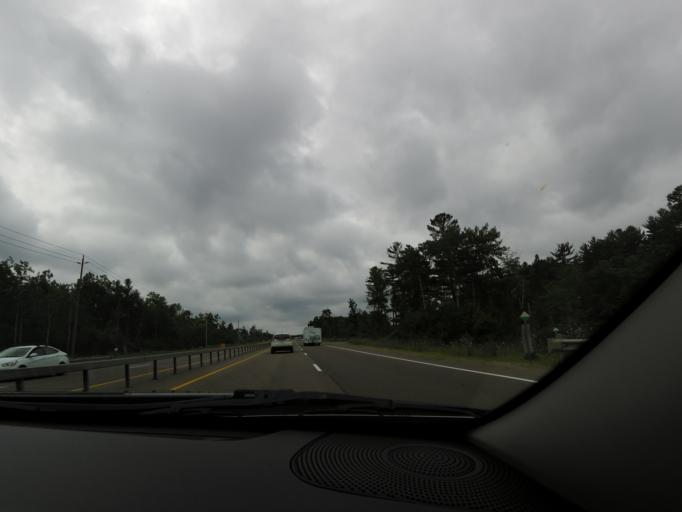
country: CA
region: Ontario
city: Gravenhurst
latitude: 44.7624
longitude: -79.3350
